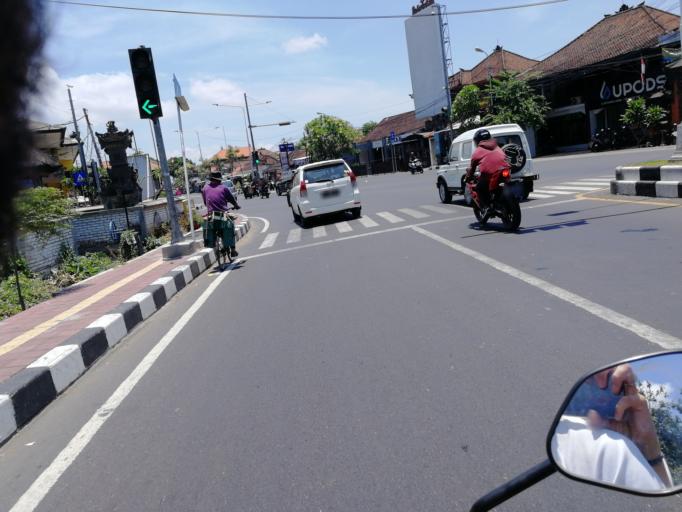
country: ID
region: Bali
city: Karyadharma
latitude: -8.6894
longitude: 115.1915
